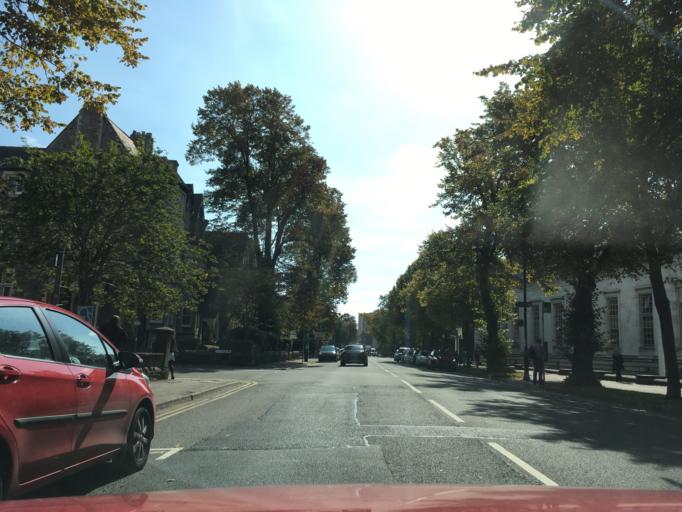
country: GB
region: Wales
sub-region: Cardiff
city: Cardiff
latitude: 51.4866
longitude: -3.1770
